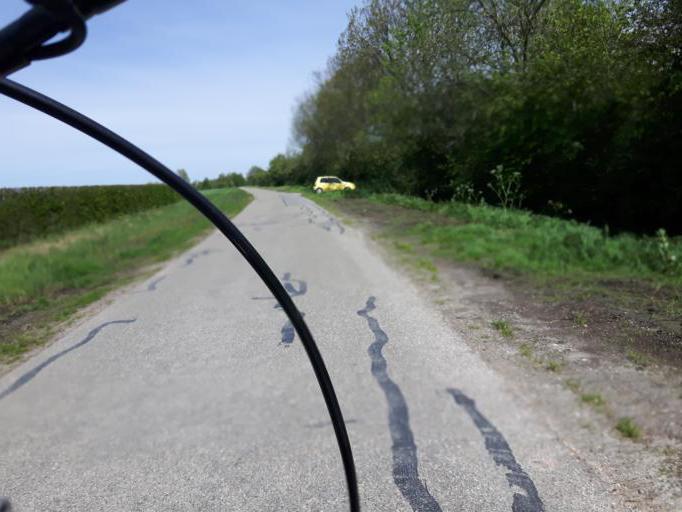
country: NL
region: Zeeland
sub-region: Gemeente Goes
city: Goes
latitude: 51.4575
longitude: 3.8813
